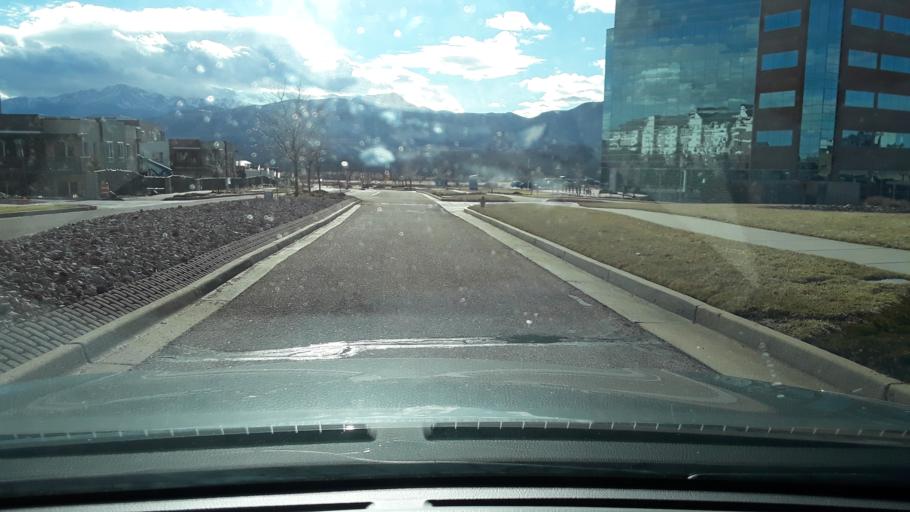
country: US
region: Colorado
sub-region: El Paso County
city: Air Force Academy
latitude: 38.9880
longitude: -104.8036
